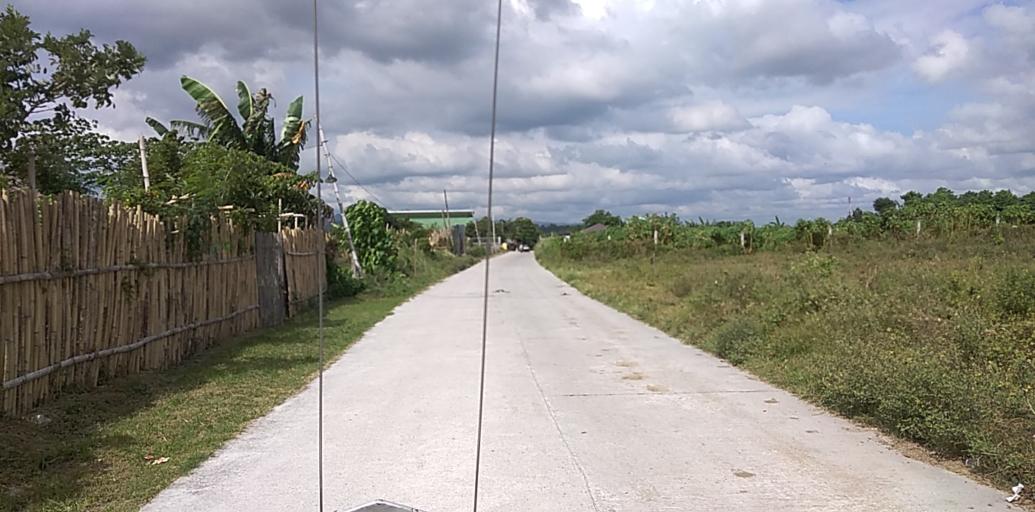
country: PH
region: Central Luzon
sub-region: Province of Pampanga
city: Porac
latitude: 15.0609
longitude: 120.5374
